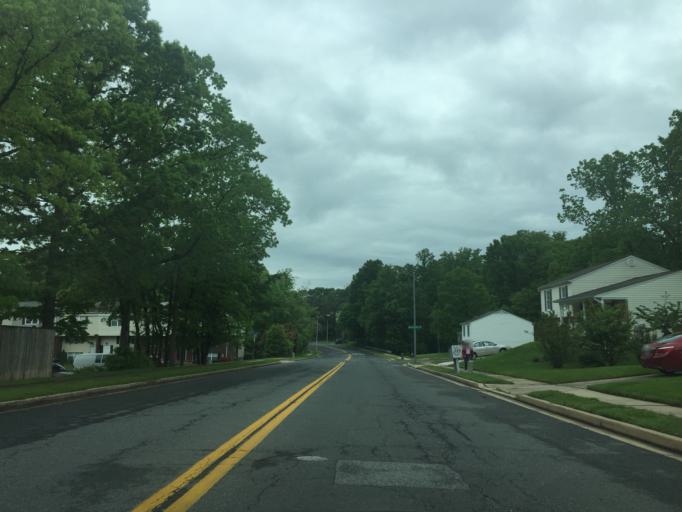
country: US
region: Maryland
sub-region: Baltimore County
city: Perry Hall
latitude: 39.3848
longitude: -76.4672
